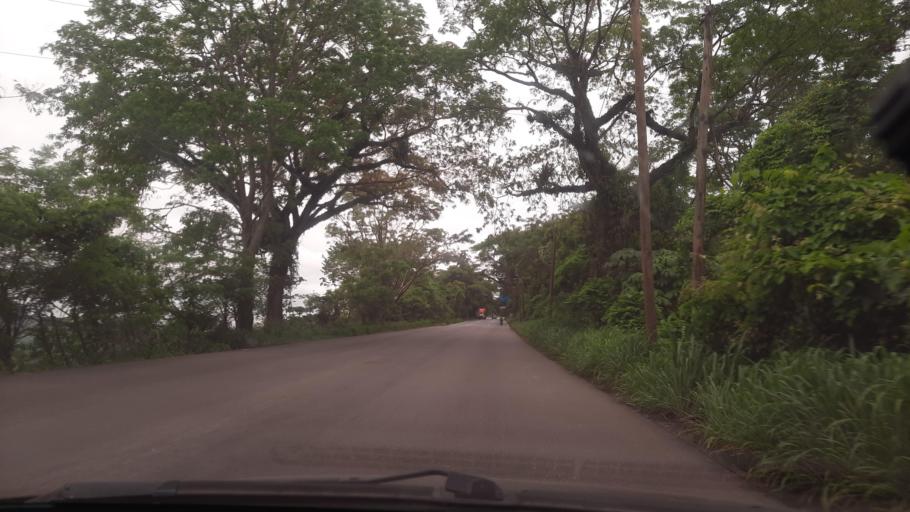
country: GT
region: Izabal
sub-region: Municipio de Los Amates
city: Los Amates
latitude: 15.2485
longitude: -89.1302
